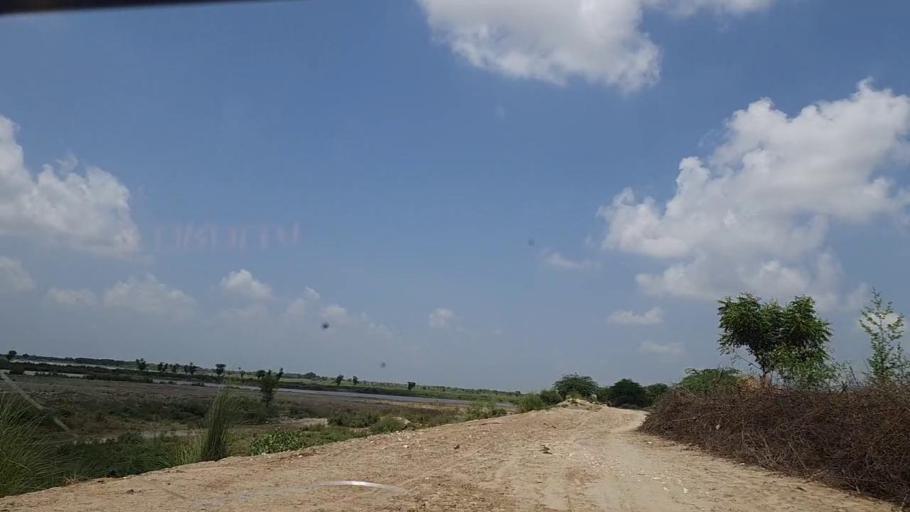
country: PK
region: Sindh
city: Tharu Shah
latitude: 26.9658
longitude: 68.0313
